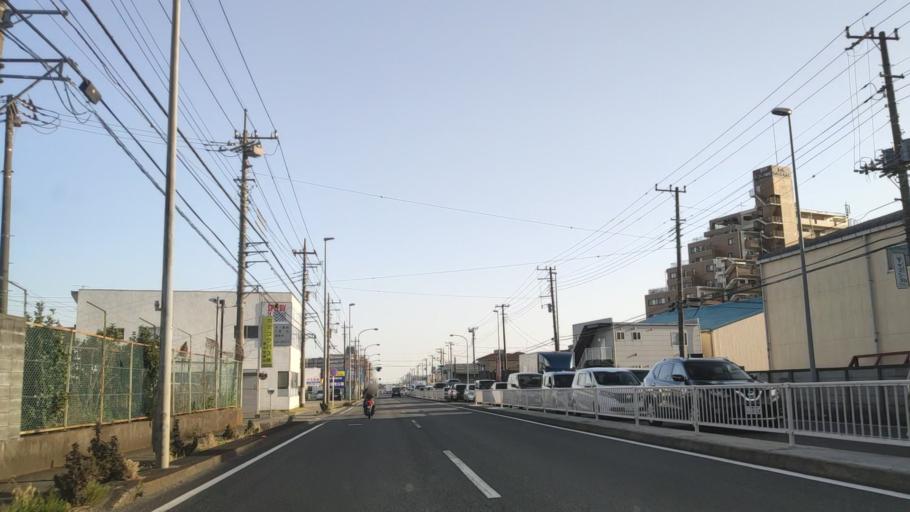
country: JP
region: Kanagawa
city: Zama
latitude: 35.4840
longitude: 139.3654
